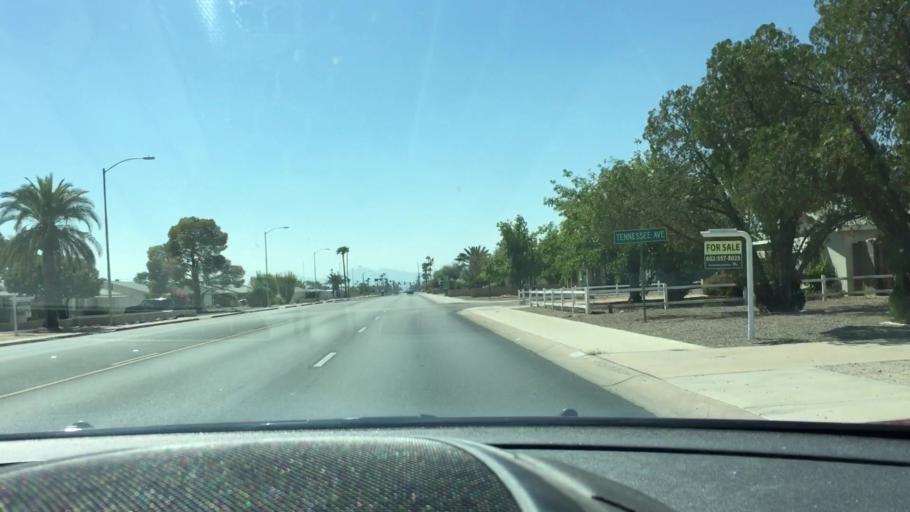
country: US
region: Arizona
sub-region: Maricopa County
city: Youngtown
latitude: 33.6000
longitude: -112.2988
